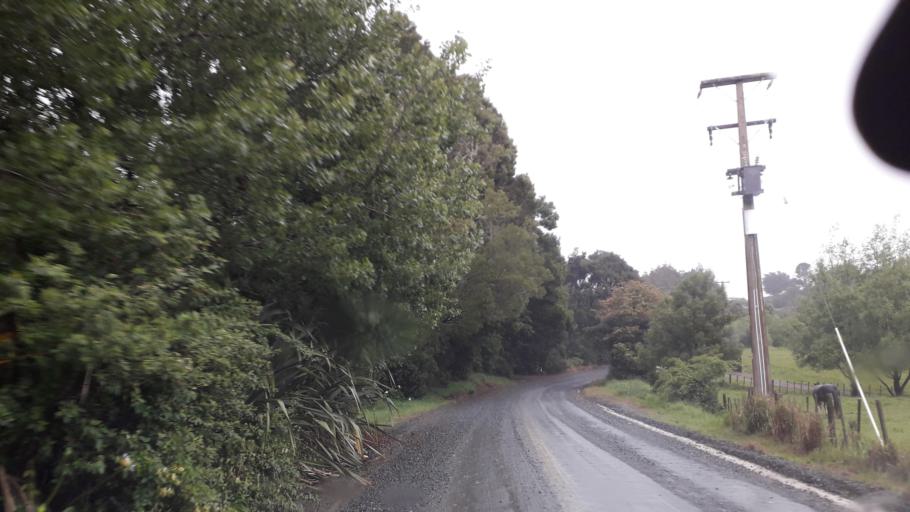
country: NZ
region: Northland
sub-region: Far North District
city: Kerikeri
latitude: -35.1205
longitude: 173.7516
